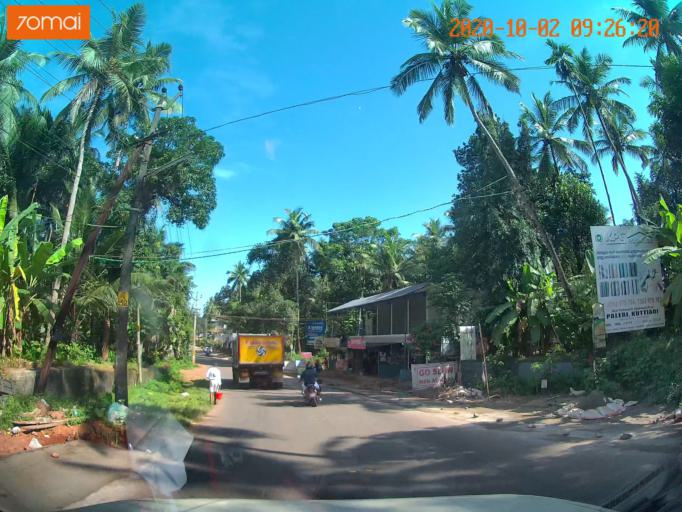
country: IN
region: Kerala
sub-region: Kozhikode
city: Naduvannur
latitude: 11.5918
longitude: 75.7669
